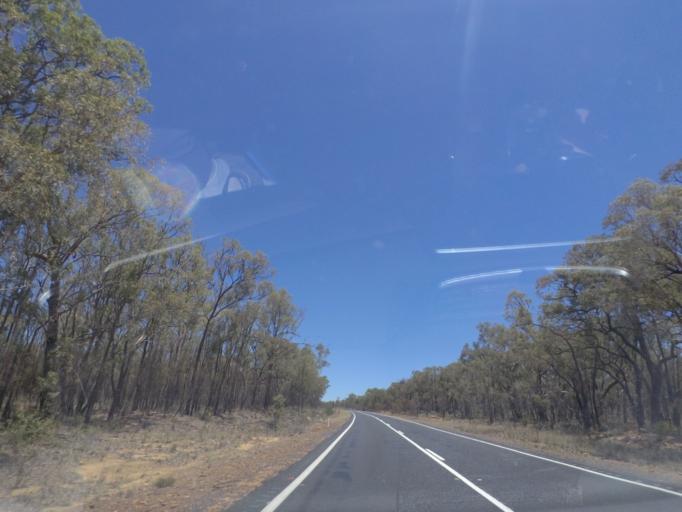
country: AU
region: New South Wales
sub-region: Warrumbungle Shire
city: Coonabarabran
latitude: -31.1776
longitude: 149.3569
